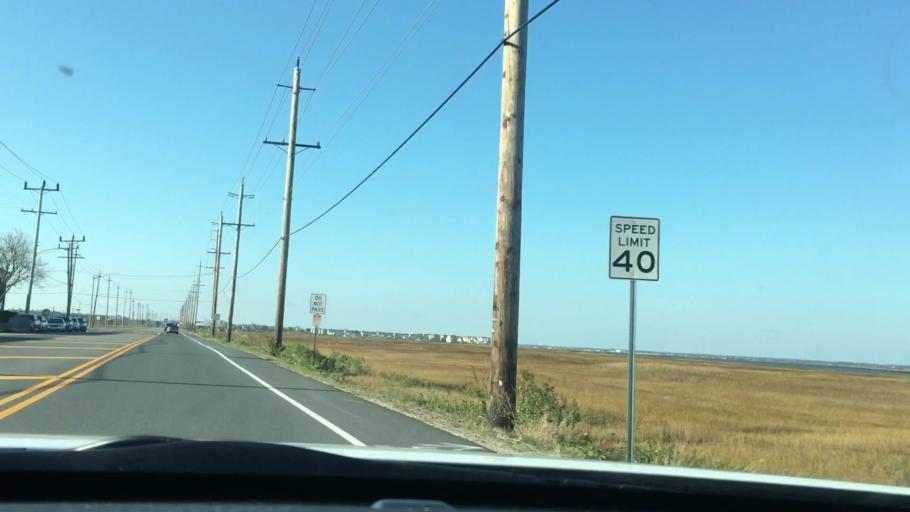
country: US
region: New Jersey
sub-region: Atlantic County
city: Ventnor City
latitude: 39.3581
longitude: -74.4669
